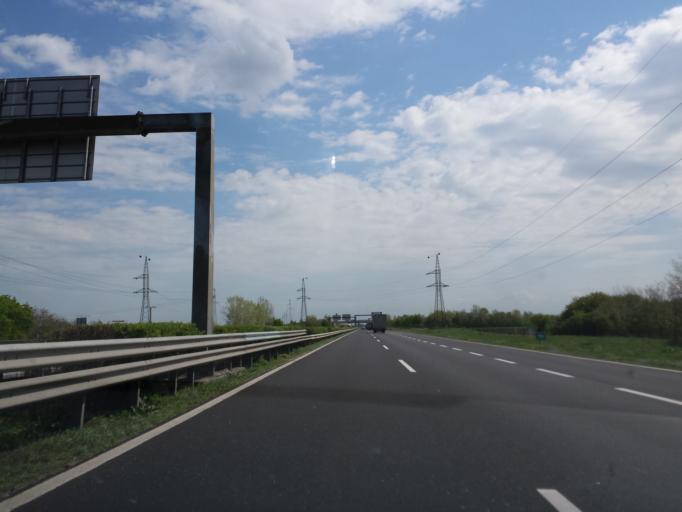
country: HU
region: Gyor-Moson-Sopron
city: Mosonmagyarovar
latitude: 47.8511
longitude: 17.2496
